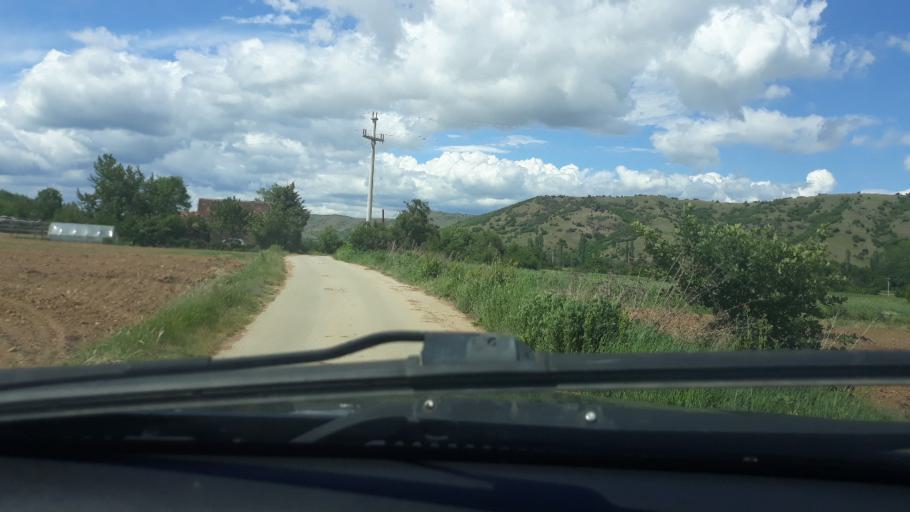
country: MK
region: Krivogastani
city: Krivogashtani
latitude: 41.3454
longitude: 21.2991
